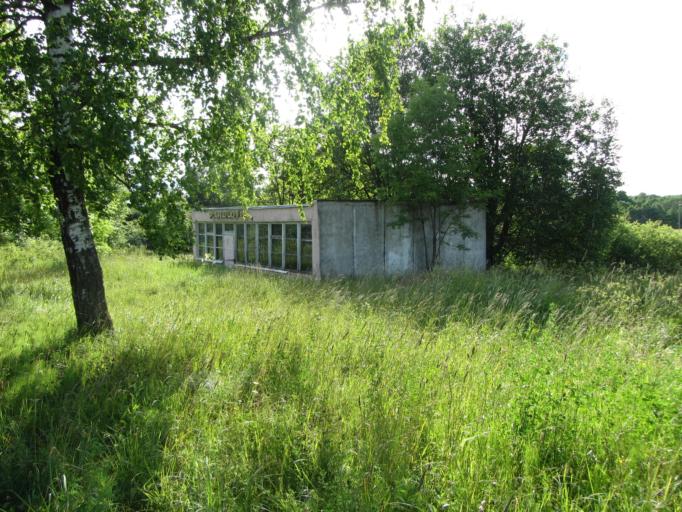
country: BY
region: Vitebsk
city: Lyntupy
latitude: 55.2290
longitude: 26.3416
